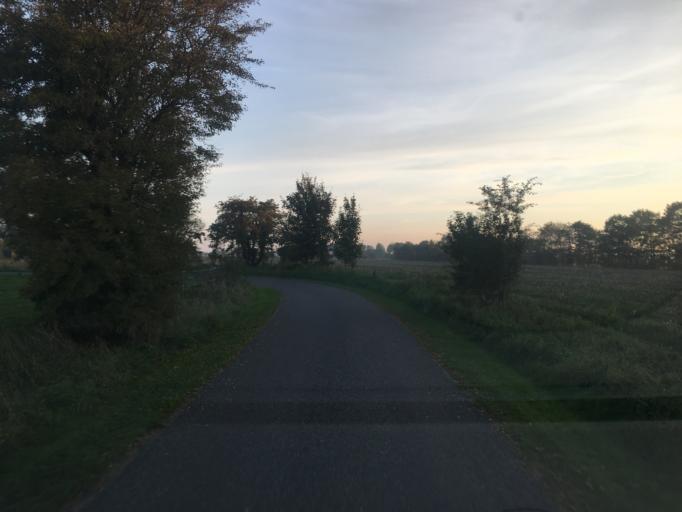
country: DK
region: South Denmark
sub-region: Tonder Kommune
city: Toftlund
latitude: 55.0358
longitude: 9.1162
